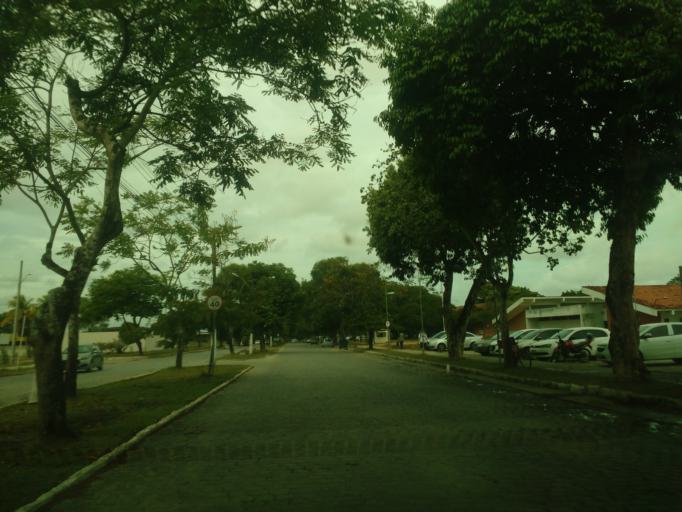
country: BR
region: Alagoas
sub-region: Satuba
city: Satuba
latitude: -9.5570
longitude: -35.7805
